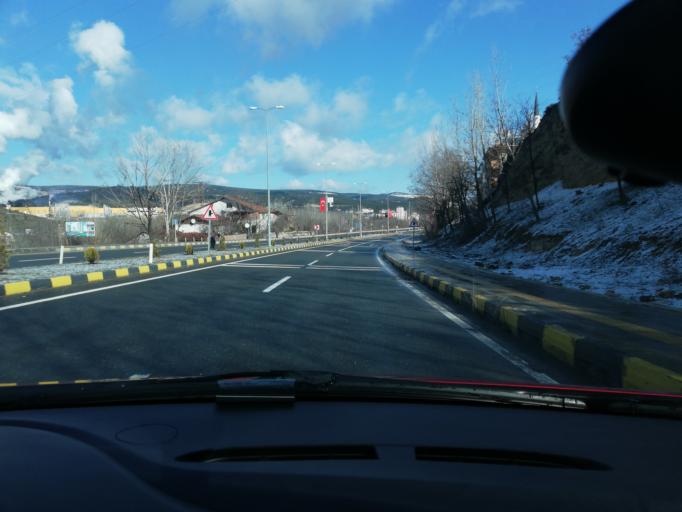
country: TR
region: Kastamonu
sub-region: Cide
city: Kastamonu
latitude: 41.3477
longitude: 33.7662
